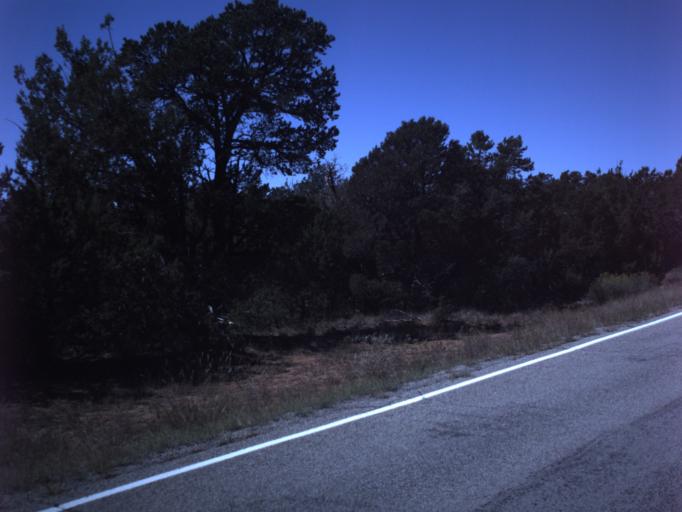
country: US
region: Utah
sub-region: San Juan County
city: Blanding
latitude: 37.5607
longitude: -109.7980
